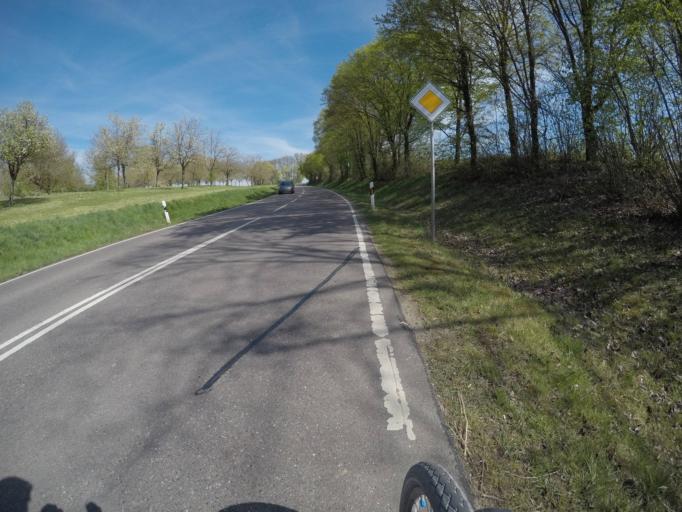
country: DE
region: Baden-Wuerttemberg
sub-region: Regierungsbezirk Stuttgart
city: Schwieberdingen
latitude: 48.8571
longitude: 9.0628
